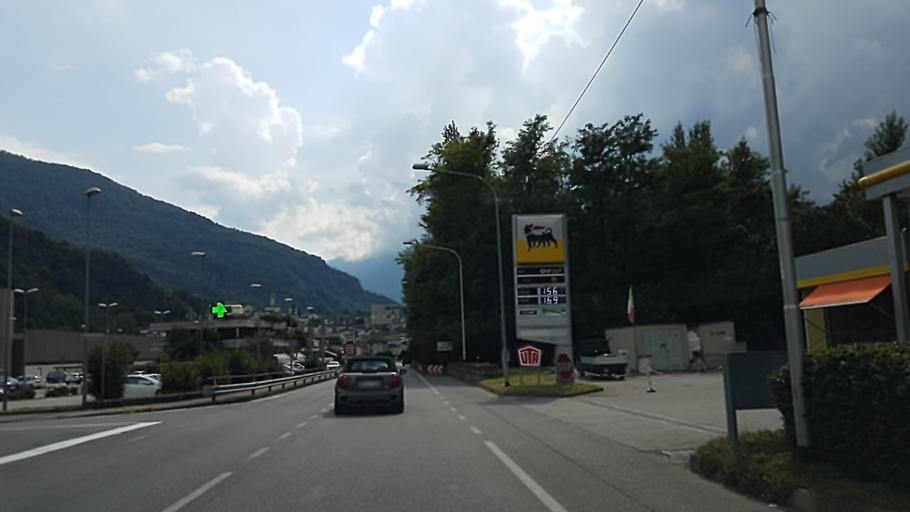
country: IT
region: Lombardy
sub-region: Provincia di Sondrio
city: Prata Centro
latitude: 46.3131
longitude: 9.3972
